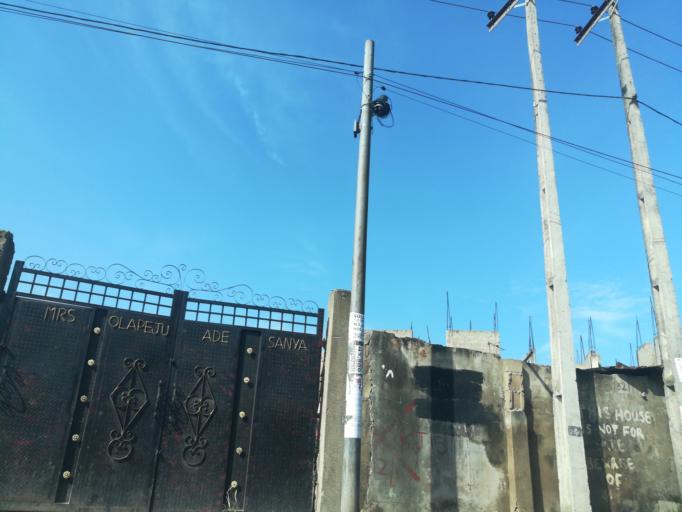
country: NG
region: Lagos
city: Ikeja
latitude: 6.6009
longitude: 3.3412
